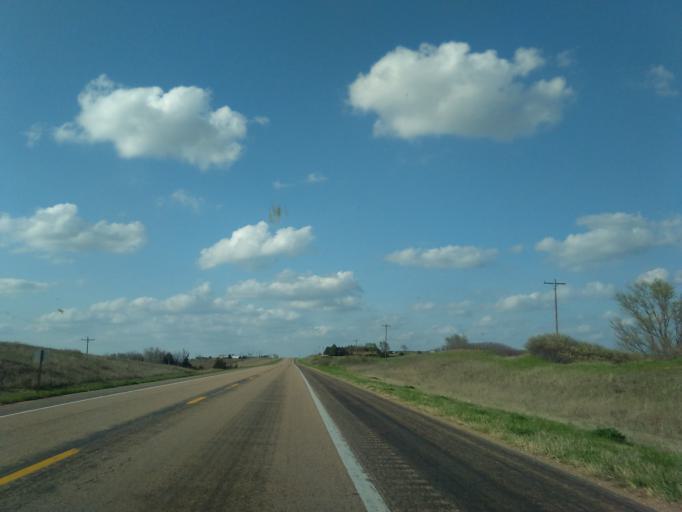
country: US
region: Nebraska
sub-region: Webster County
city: Red Cloud
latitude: 40.1334
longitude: -98.5189
